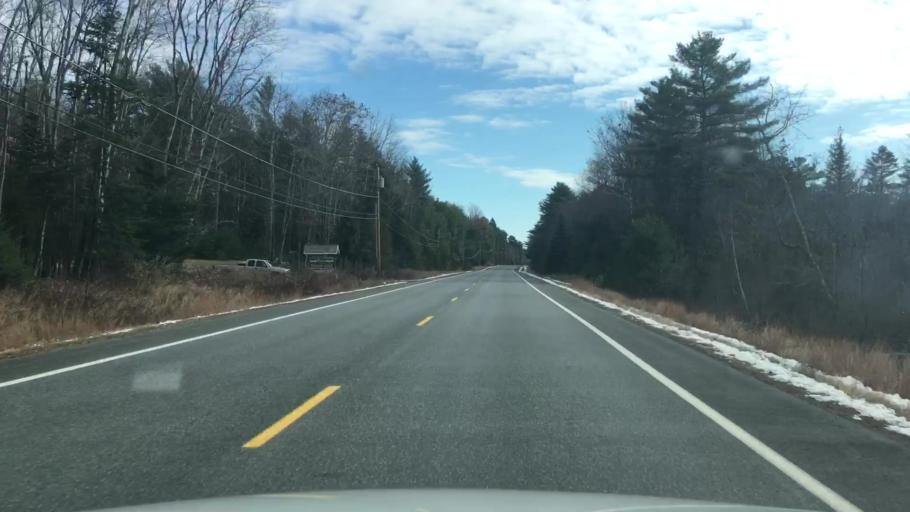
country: US
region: Maine
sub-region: Kennebec County
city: Wayne
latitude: 44.3474
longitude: -70.0430
